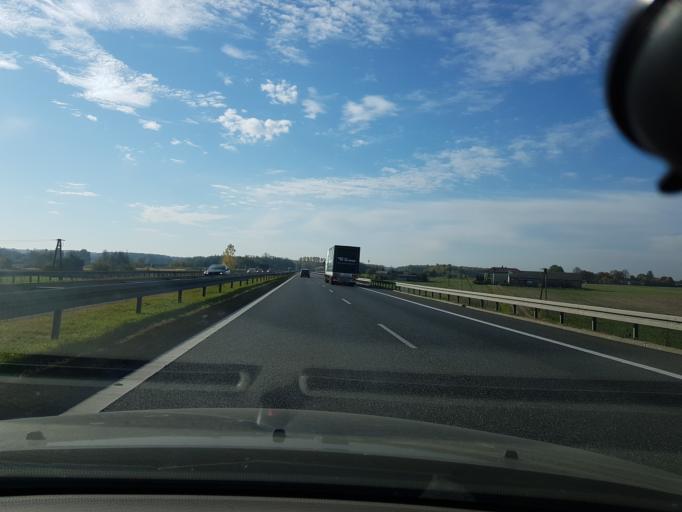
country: PL
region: Masovian Voivodeship
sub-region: Powiat zyrardowski
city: Mszczonow
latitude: 51.9660
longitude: 20.5008
